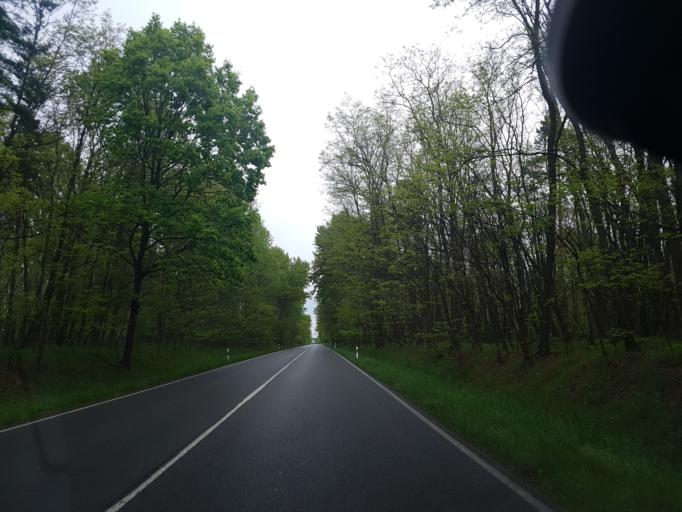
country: DE
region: Brandenburg
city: Neupetershain
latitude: 51.5937
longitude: 14.1166
